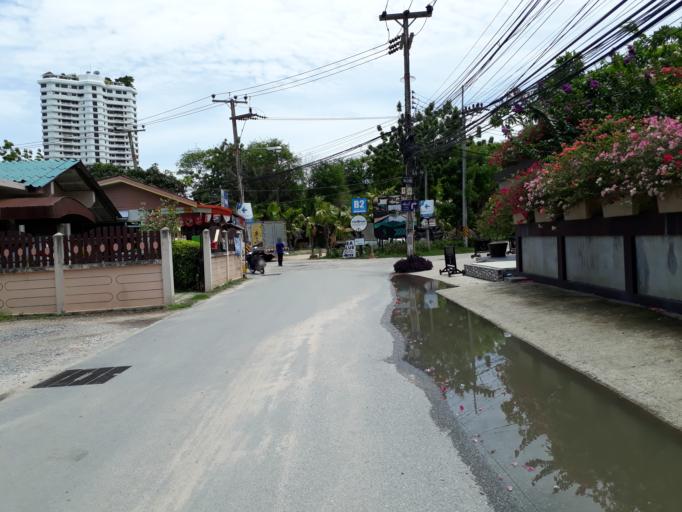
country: TH
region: Chon Buri
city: Phatthaya
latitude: 12.8448
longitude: 100.9066
